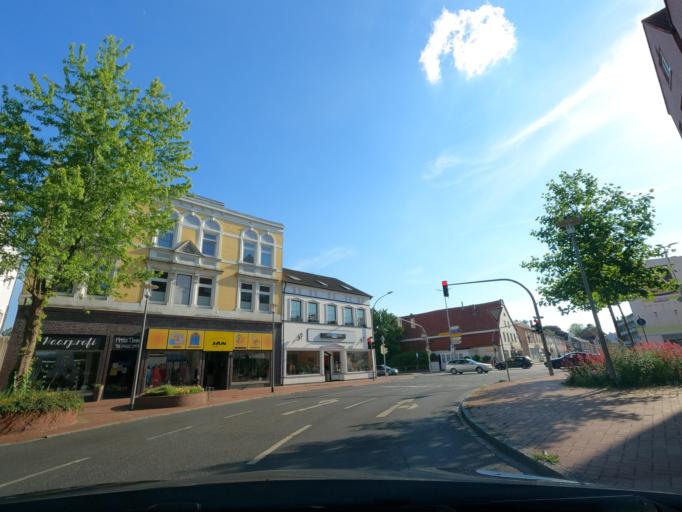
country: DE
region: Schleswig-Holstein
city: Uetersen
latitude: 53.6842
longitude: 9.6634
